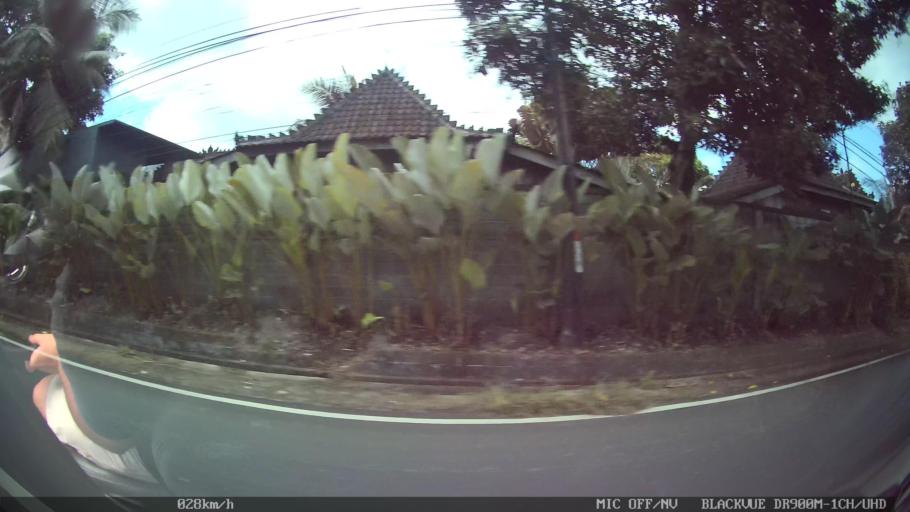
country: ID
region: Bali
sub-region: Kabupaten Gianyar
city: Ubud
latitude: -8.5397
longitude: 115.2819
